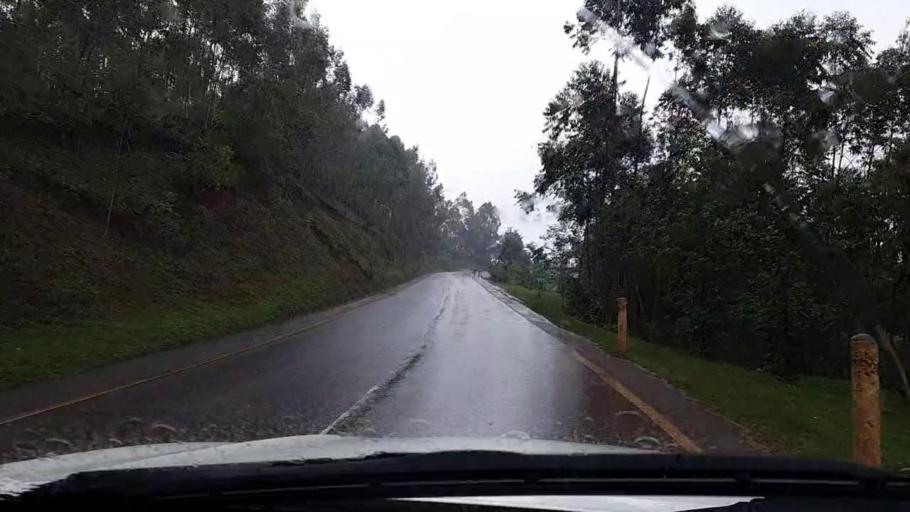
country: RW
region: Western Province
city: Cyangugu
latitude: -2.4617
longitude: 29.0016
